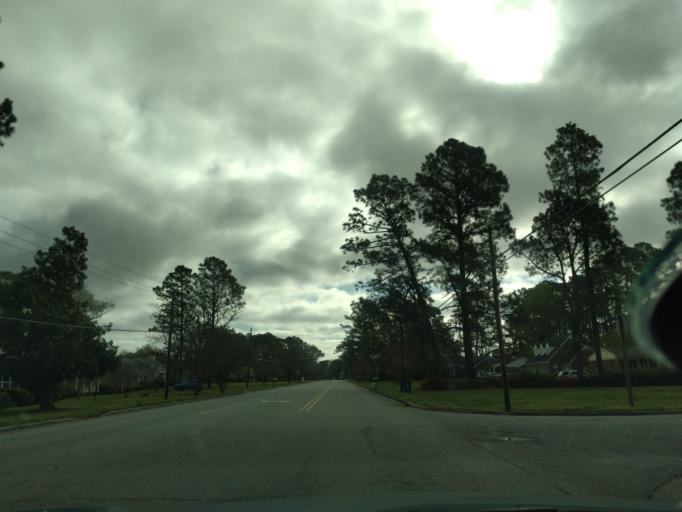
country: US
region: North Carolina
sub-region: Chowan County
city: Edenton
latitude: 36.0568
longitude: -76.6371
